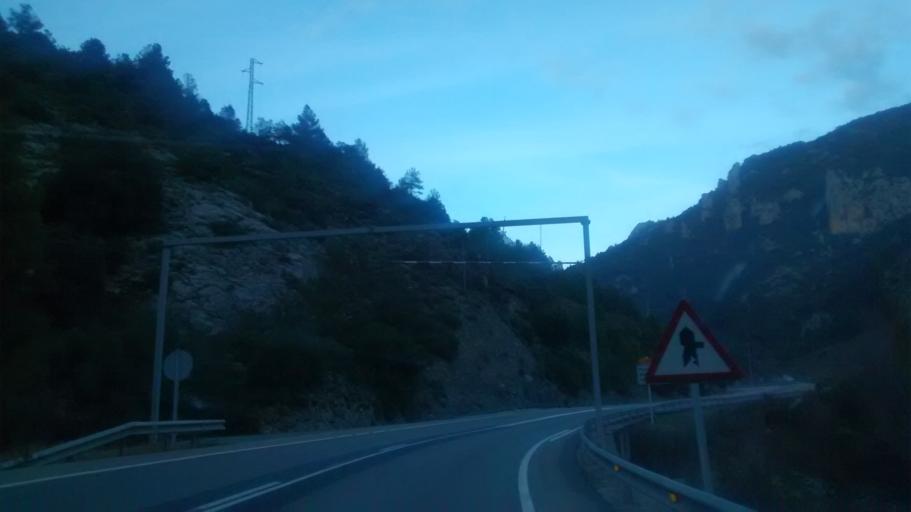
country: ES
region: Catalonia
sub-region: Provincia de Lleida
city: Coll de Nargo
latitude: 42.2460
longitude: 1.3443
